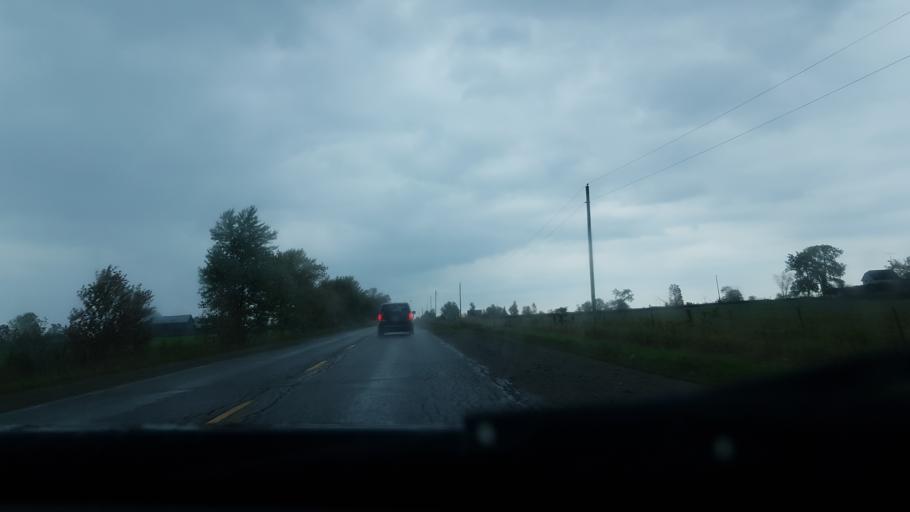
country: CA
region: Ontario
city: Omemee
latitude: 44.3798
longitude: -78.6180
